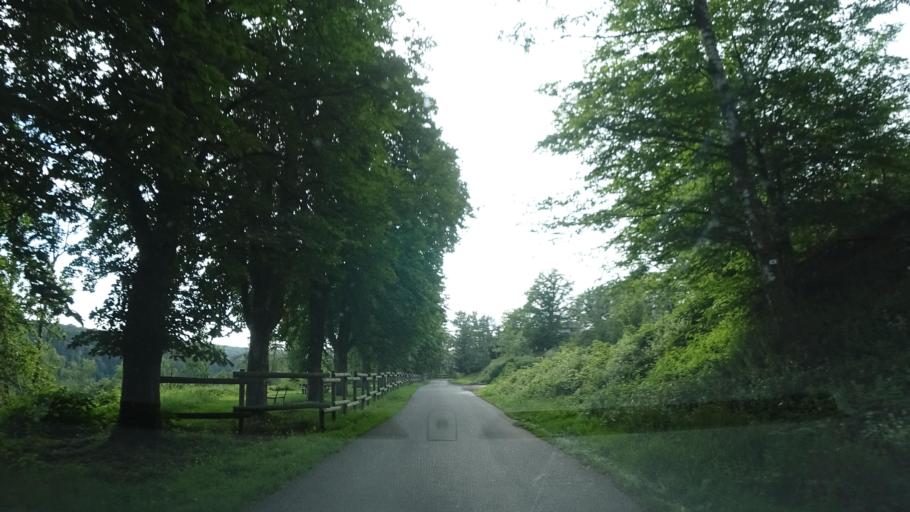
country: BE
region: Wallonia
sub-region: Province du Luxembourg
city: Herbeumont
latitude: 49.7733
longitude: 5.2444
